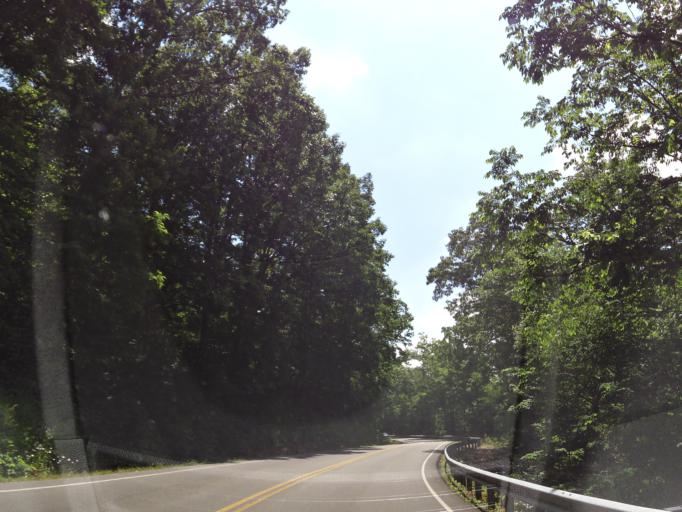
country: US
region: Tennessee
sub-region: Bledsoe County
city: Pikeville
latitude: 35.5909
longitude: -85.1533
